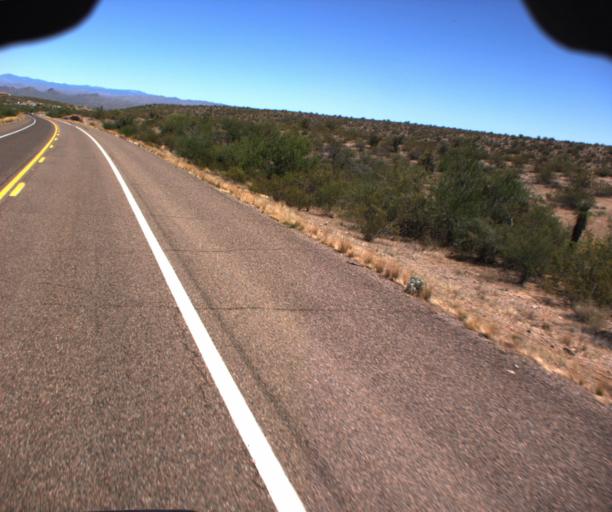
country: US
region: Arizona
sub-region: Maricopa County
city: Wickenburg
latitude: 33.9579
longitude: -112.8381
